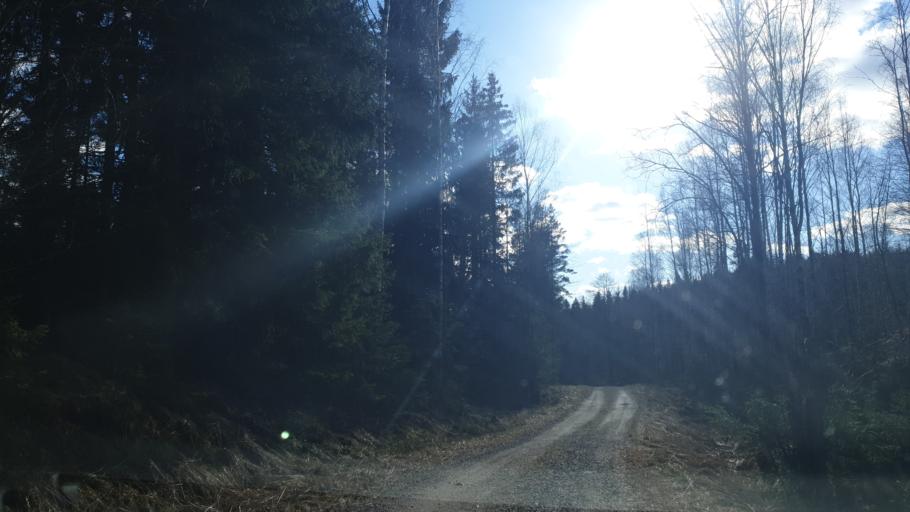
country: SE
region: OErebro
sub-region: Orebro Kommun
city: Garphyttan
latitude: 59.3740
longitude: 14.9767
